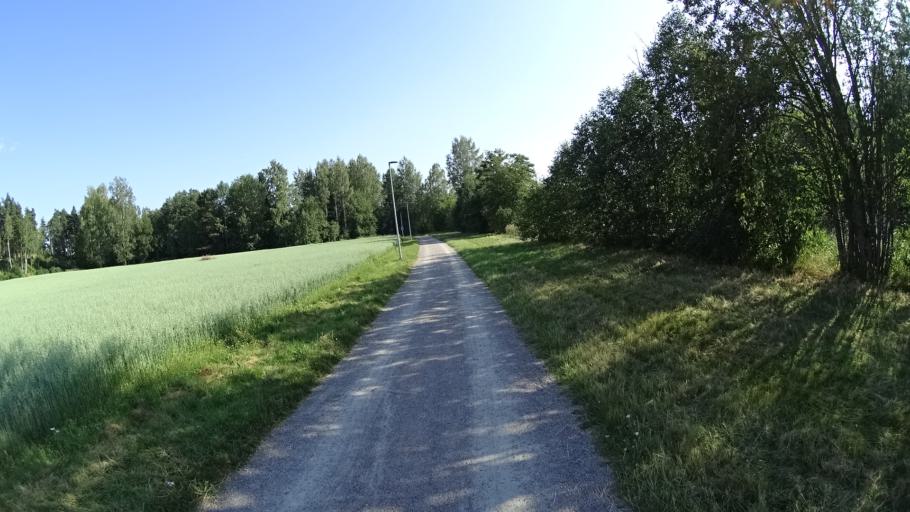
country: FI
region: Uusimaa
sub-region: Porvoo
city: Porvoo
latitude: 60.4007
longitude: 25.6446
